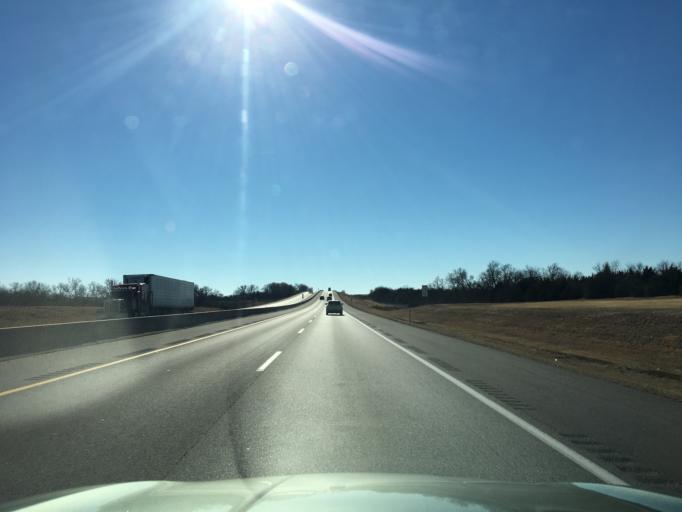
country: US
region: Kansas
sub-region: Sumner County
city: Belle Plaine
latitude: 37.3576
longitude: -97.3222
